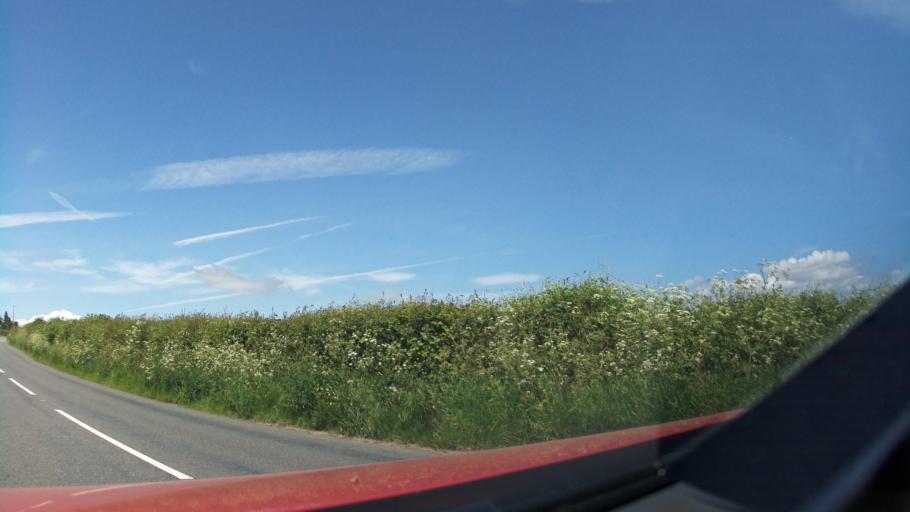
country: GB
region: Wales
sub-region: Monmouthshire
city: Caldicot
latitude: 51.6354
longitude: -2.7477
